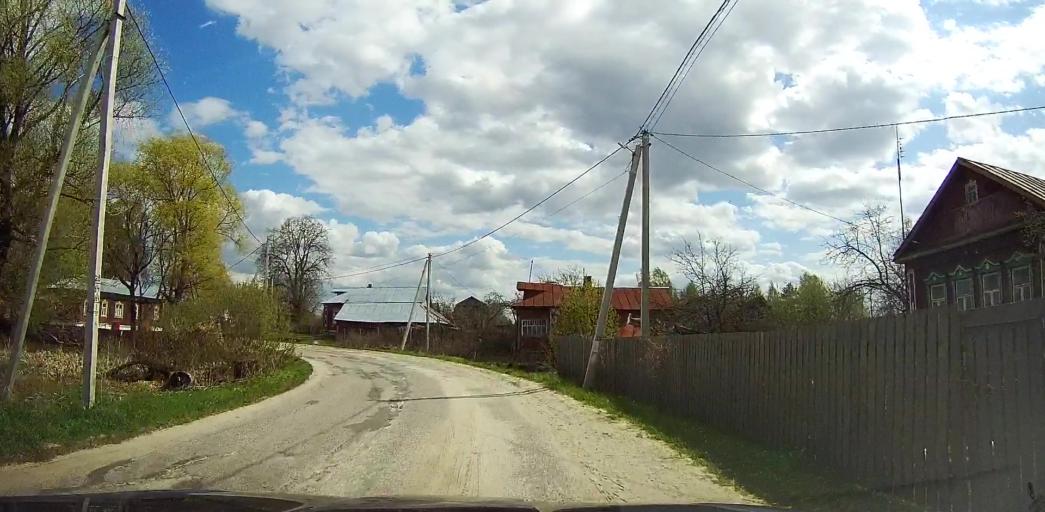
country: RU
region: Moskovskaya
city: Davydovo
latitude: 55.6389
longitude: 38.7780
